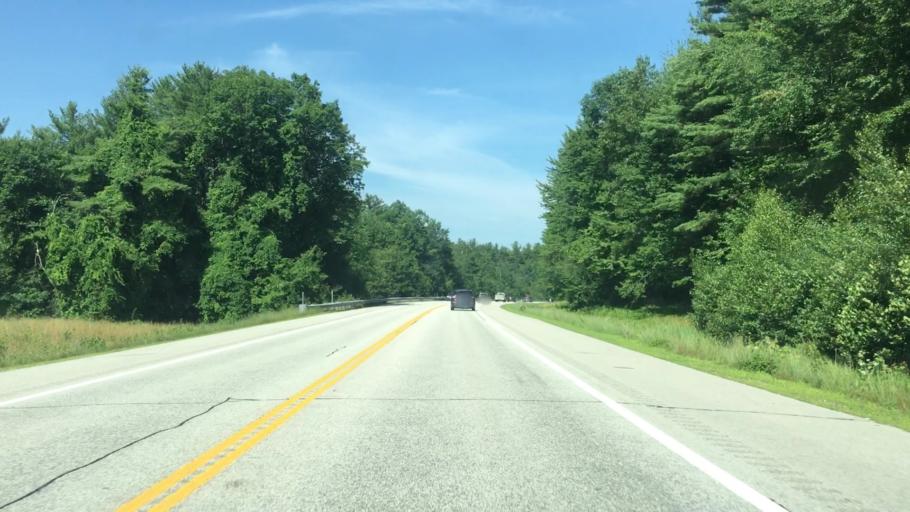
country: US
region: New Hampshire
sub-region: Merrimack County
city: Henniker
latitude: 43.1854
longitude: -71.7972
